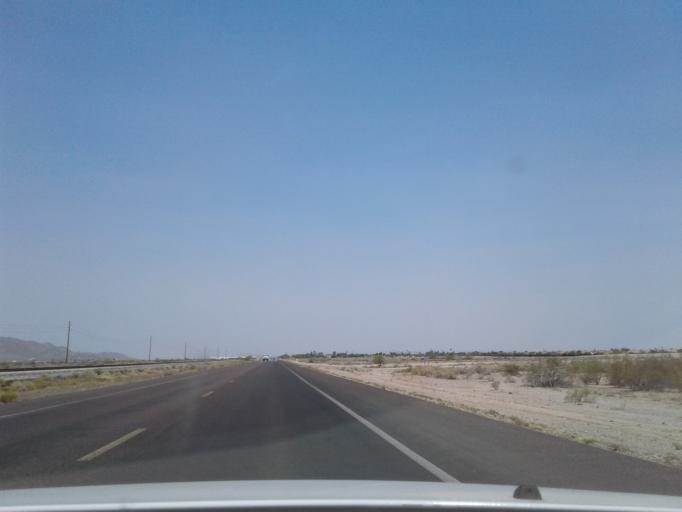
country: US
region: Arizona
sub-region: Pinal County
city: Arizona City
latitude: 32.8018
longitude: -111.6352
